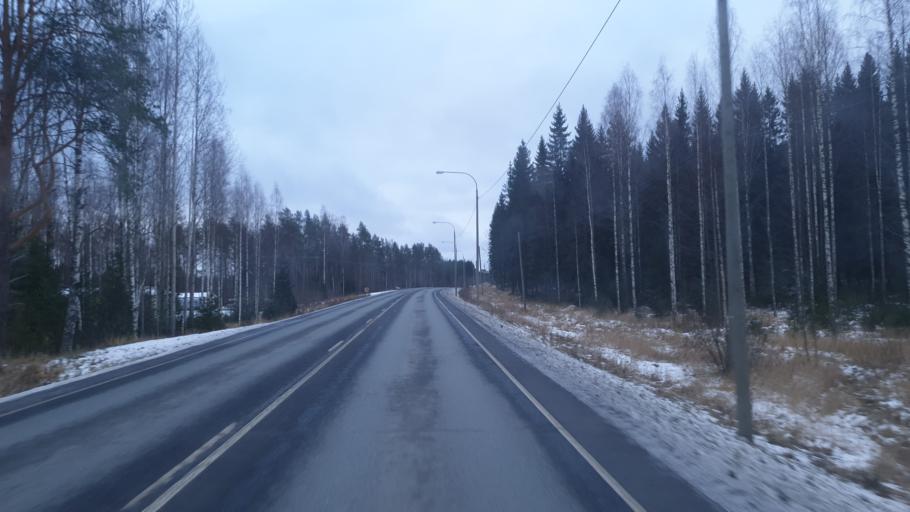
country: FI
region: Northern Savo
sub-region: Varkaus
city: Leppaevirta
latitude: 62.5382
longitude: 27.6400
